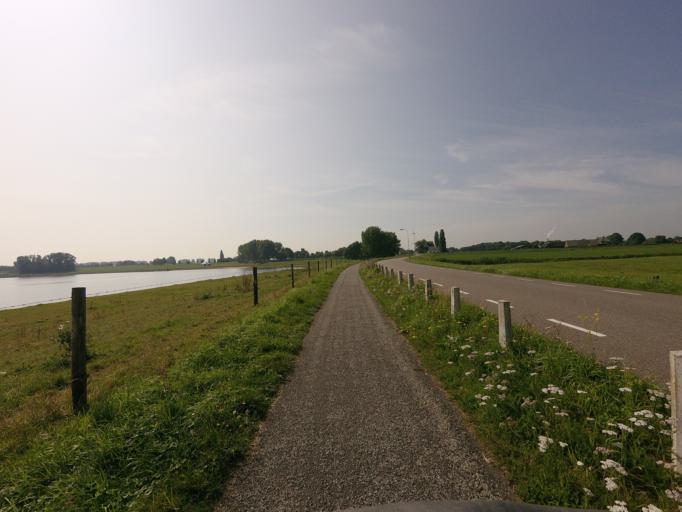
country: NL
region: Gelderland
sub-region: Gemeente Rheden
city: Rheden
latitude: 51.9895
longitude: 6.0280
